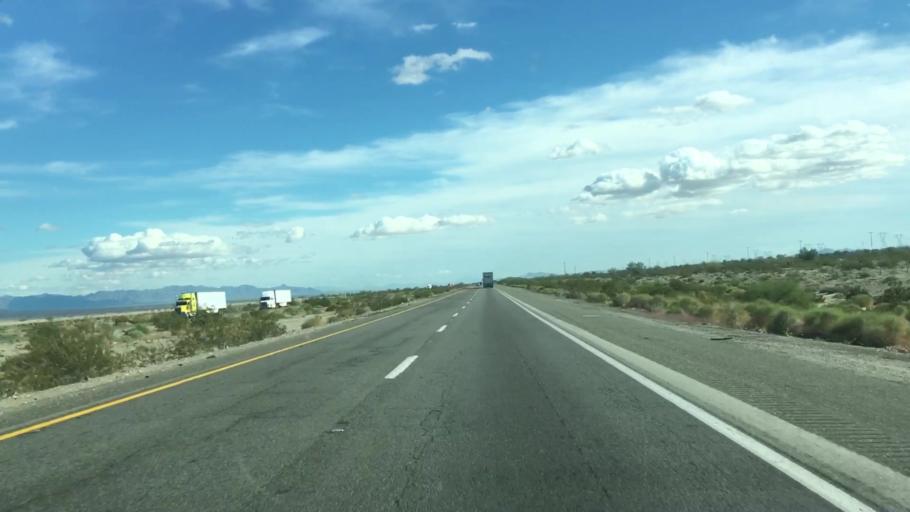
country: US
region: California
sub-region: Imperial County
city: Niland
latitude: 33.6914
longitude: -115.2745
